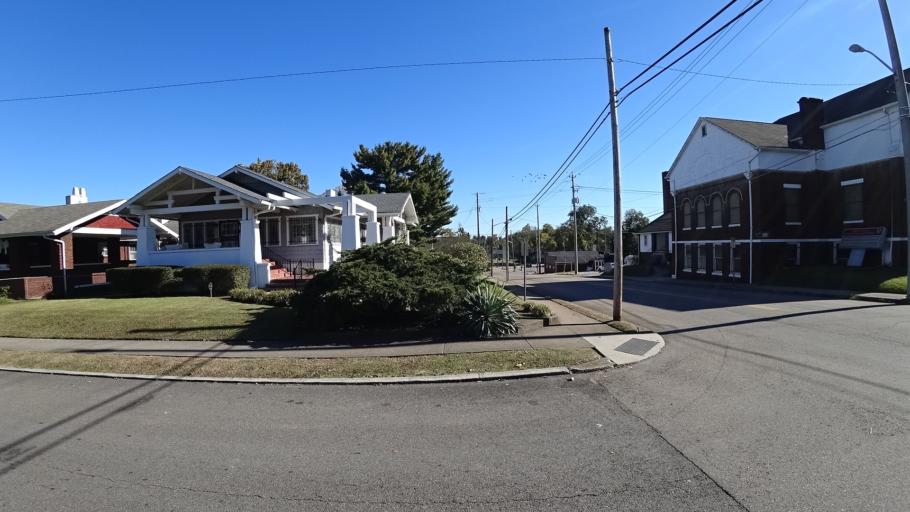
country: US
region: Tennessee
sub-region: Knox County
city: Knoxville
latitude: 35.9836
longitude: -83.8944
